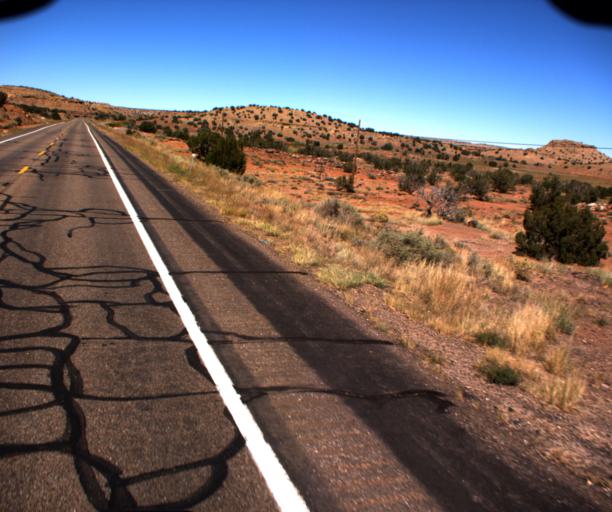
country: US
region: Arizona
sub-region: Apache County
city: Saint Johns
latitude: 34.3707
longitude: -109.3954
